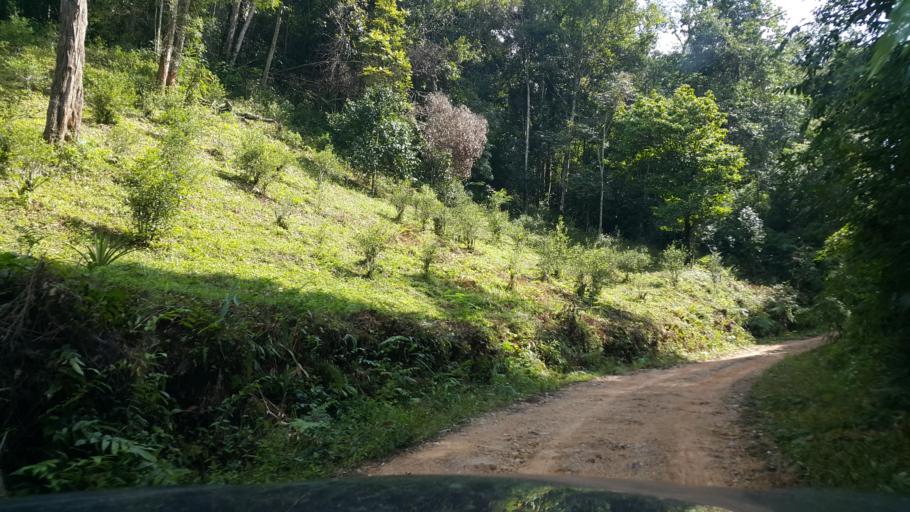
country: TH
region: Chiang Mai
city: Phrao
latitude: 19.1040
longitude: 99.2715
